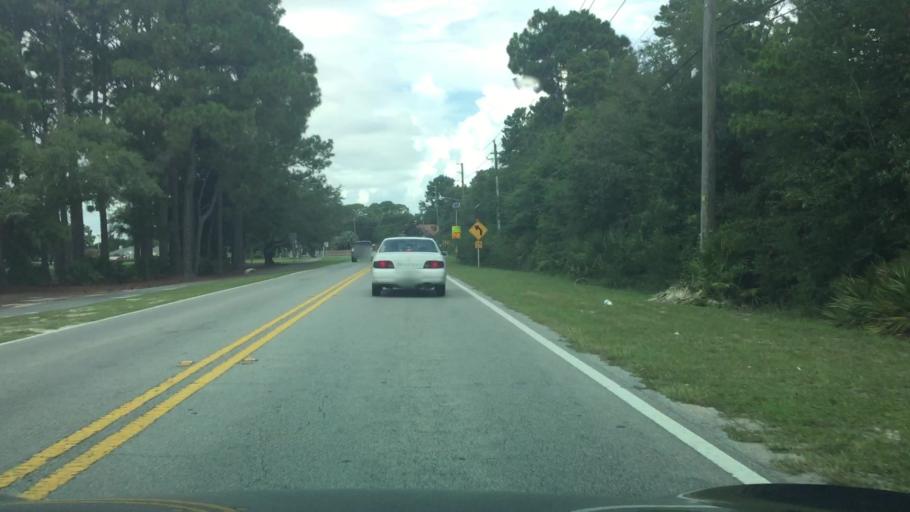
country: US
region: Florida
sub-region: Bay County
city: Upper Grand Lagoon
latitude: 30.1575
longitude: -85.7329
